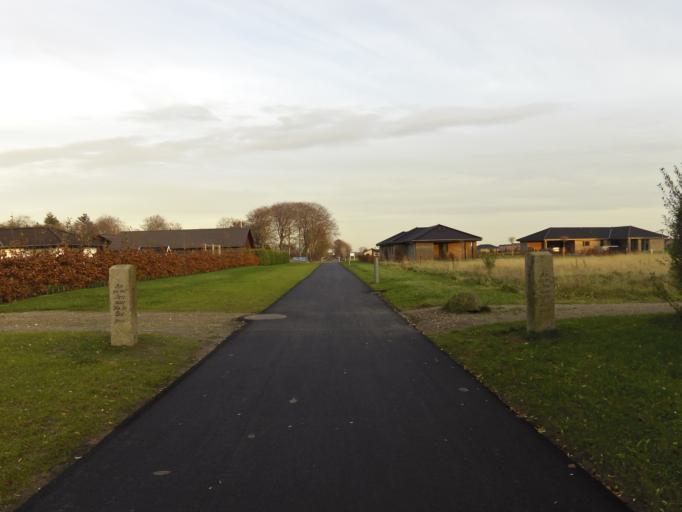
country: DK
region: South Denmark
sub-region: Vejen Kommune
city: Vejen
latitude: 55.4586
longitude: 9.1090
